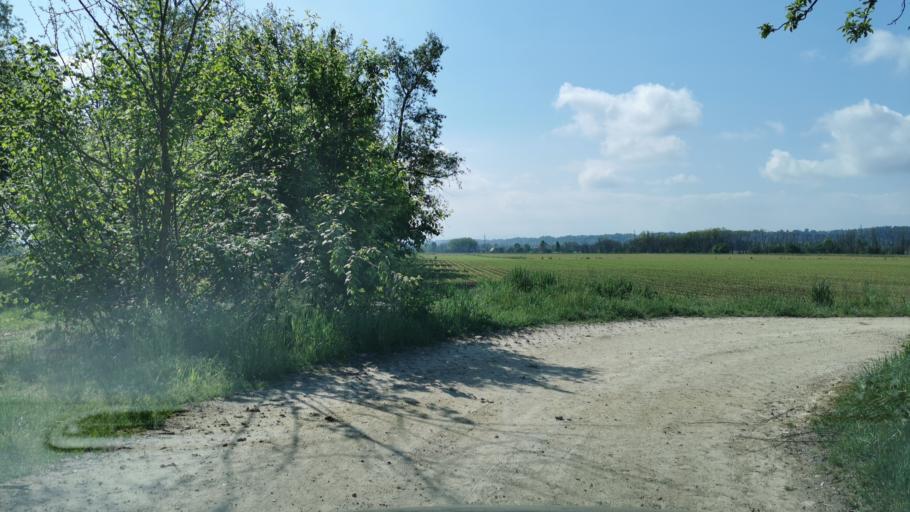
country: IT
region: Piedmont
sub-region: Provincia di Torino
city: Front
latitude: 45.2837
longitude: 7.7010
